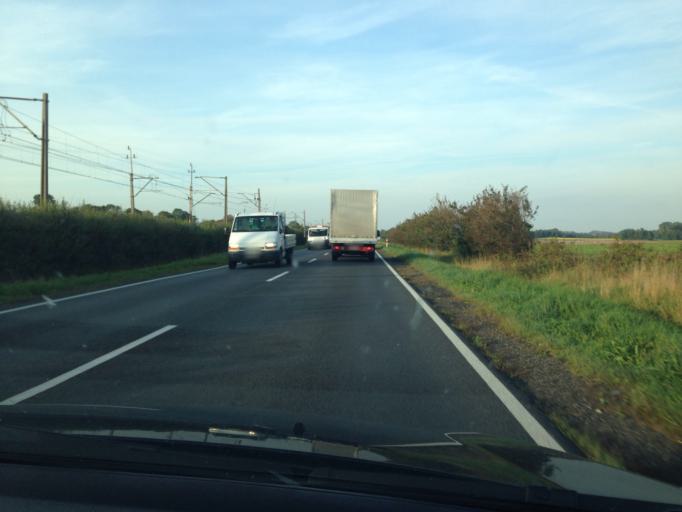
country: PL
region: Greater Poland Voivodeship
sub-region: Powiat gnieznienski
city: Trzemeszno
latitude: 52.5957
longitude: 17.8932
